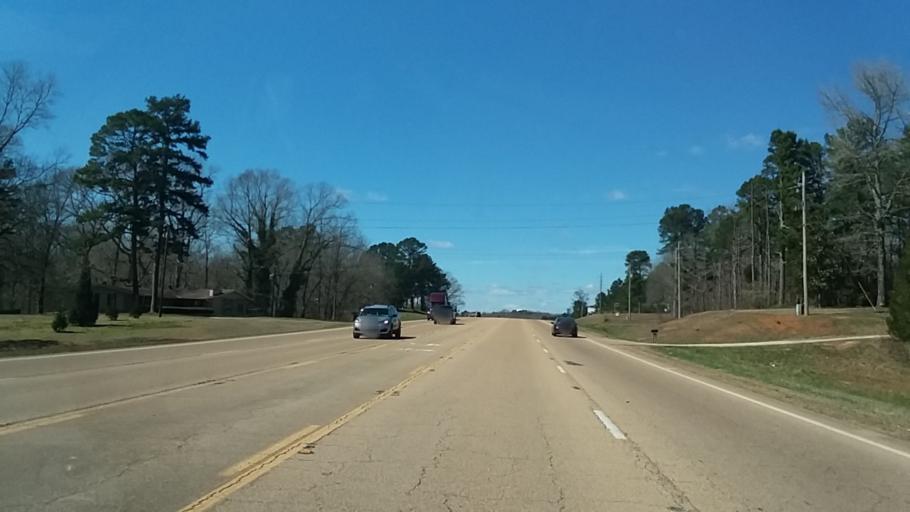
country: US
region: Mississippi
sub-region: Alcorn County
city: Farmington
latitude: 34.8957
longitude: -88.4694
